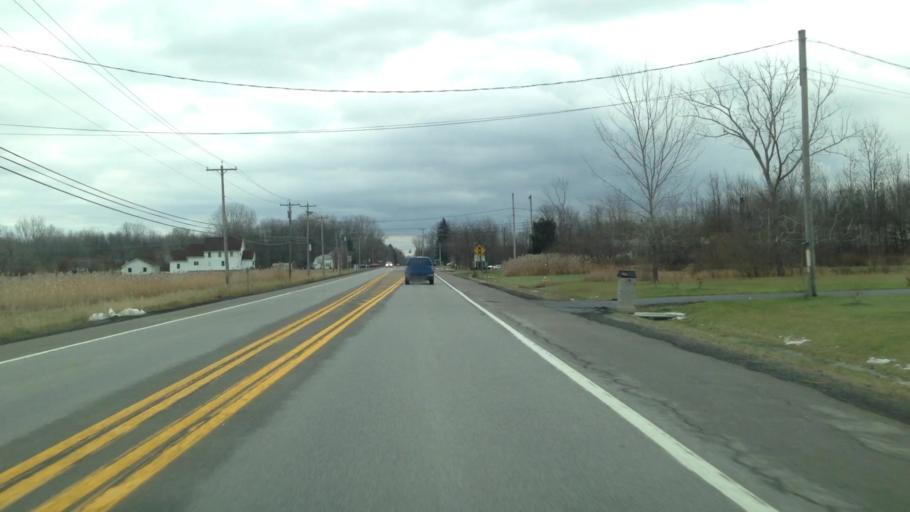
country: US
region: New York
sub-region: Erie County
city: Akron
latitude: 42.9983
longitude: -78.4819
